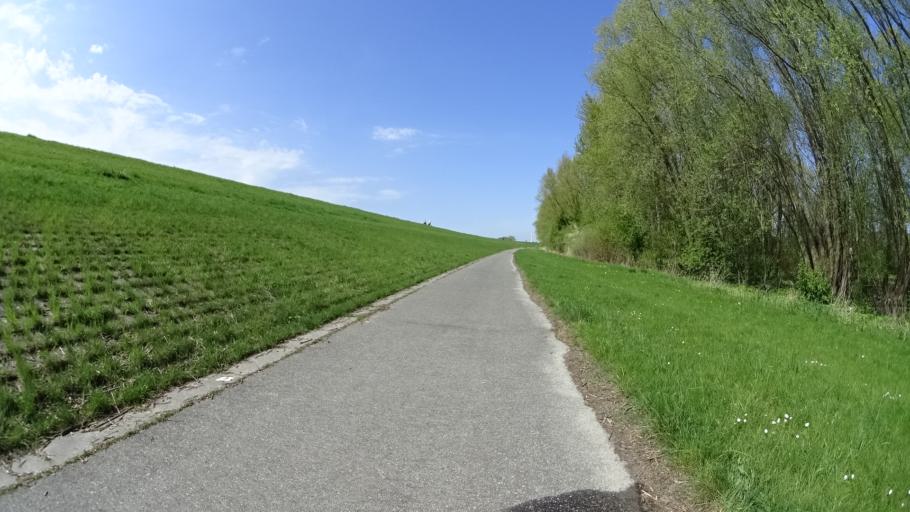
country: DE
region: Lower Saxony
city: Neu Wulmstorf
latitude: 53.5406
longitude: 9.7759
